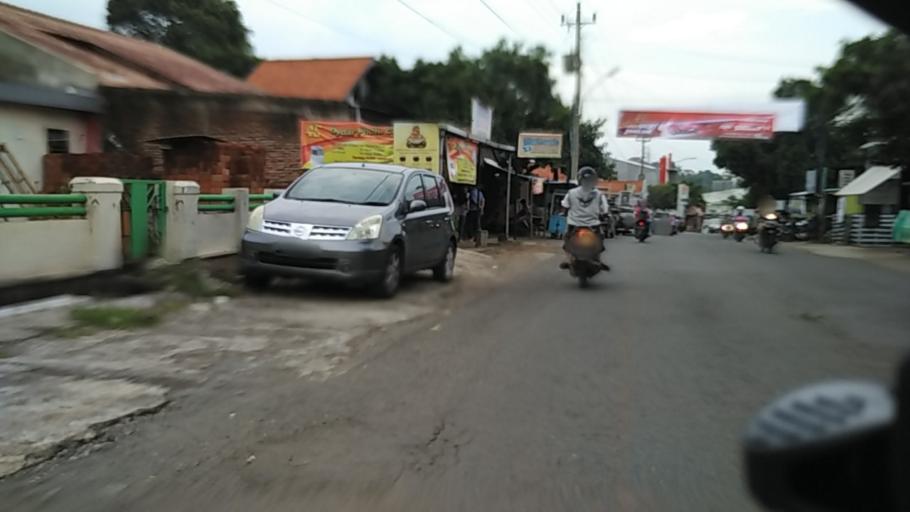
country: ID
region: Central Java
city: Semarang
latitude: -7.0570
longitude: 110.4289
